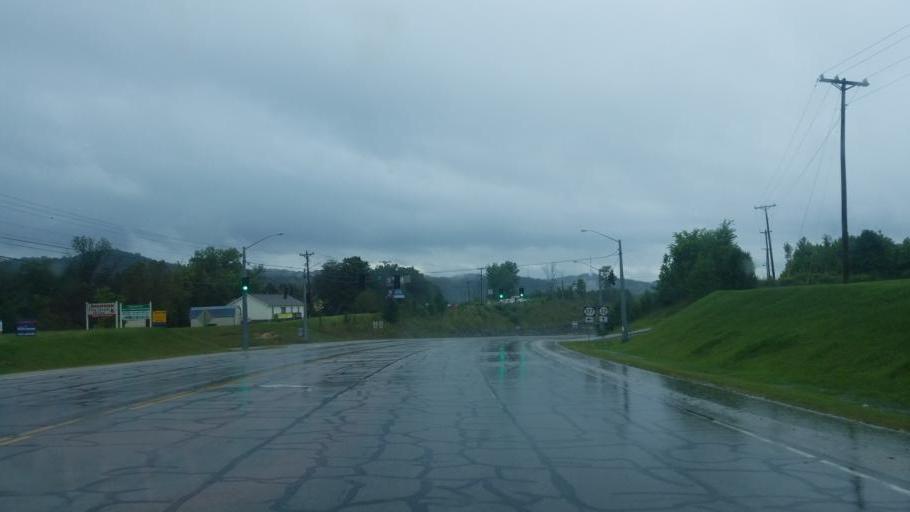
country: US
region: Kentucky
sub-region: Rowan County
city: Morehead
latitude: 38.2054
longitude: -83.4733
